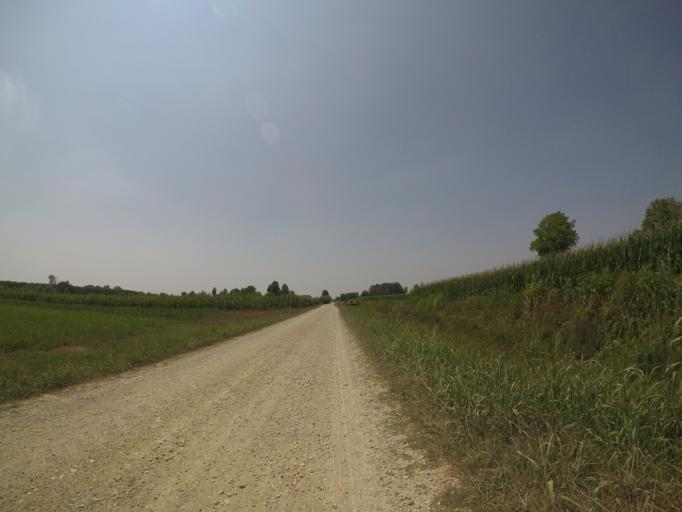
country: IT
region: Friuli Venezia Giulia
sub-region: Provincia di Udine
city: Talmassons
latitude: 45.9162
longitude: 13.1282
